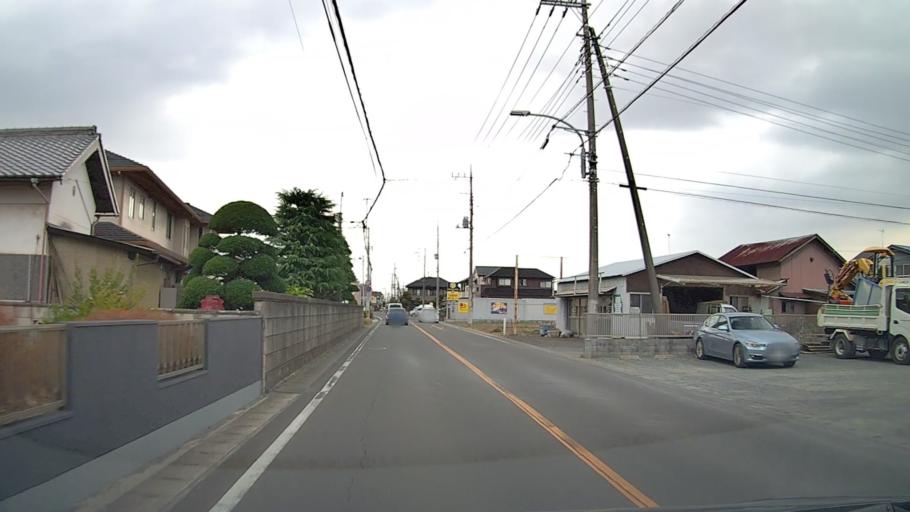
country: JP
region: Saitama
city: Shiki
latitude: 35.8443
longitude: 139.5661
